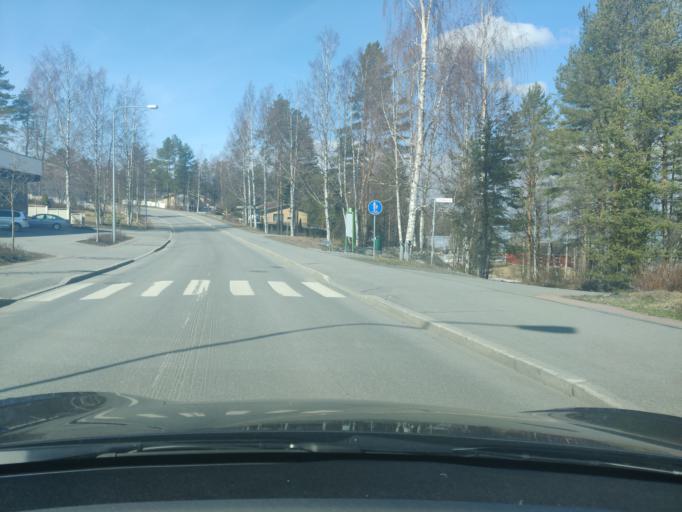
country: FI
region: Northern Savo
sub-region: Kuopio
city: Vehmersalmi
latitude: 62.9142
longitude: 28.1595
